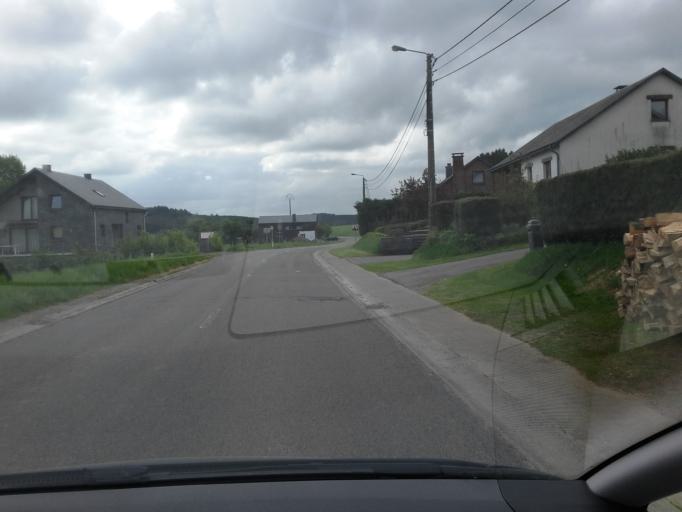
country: BE
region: Wallonia
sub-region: Province du Luxembourg
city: Bertrix
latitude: 49.8304
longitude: 5.3090
